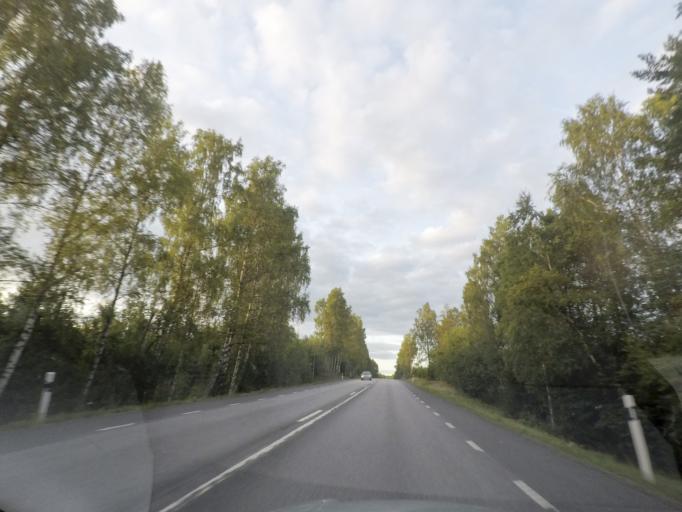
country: SE
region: OErebro
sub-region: Hallefors Kommun
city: Haellefors
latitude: 59.7554
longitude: 14.5118
